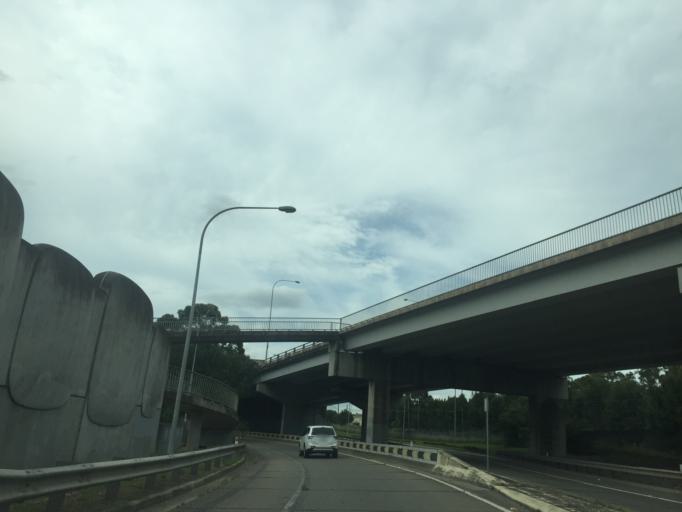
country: AU
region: New South Wales
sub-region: Parramatta
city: Granville
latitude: -33.8286
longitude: 151.0203
